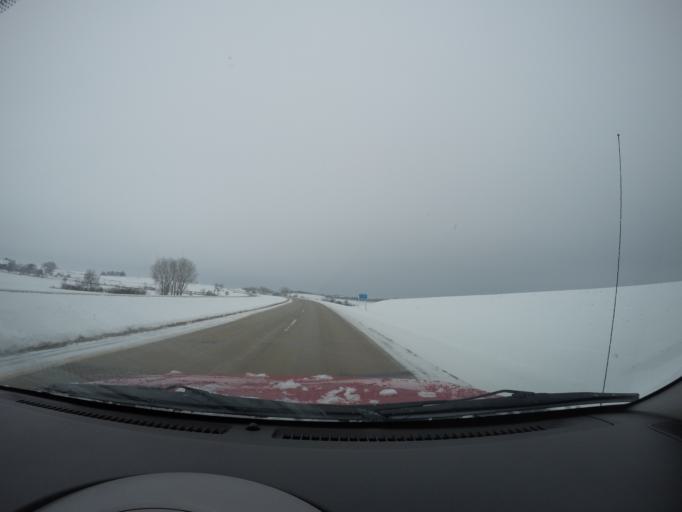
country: US
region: Minnesota
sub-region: Olmsted County
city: Rochester
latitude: 43.9708
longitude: -92.4022
